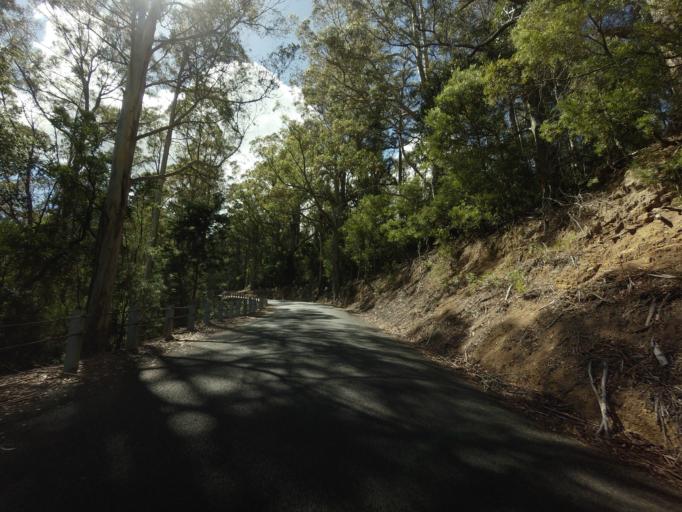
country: AU
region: Tasmania
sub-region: Break O'Day
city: St Helens
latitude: -41.6385
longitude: 148.2426
